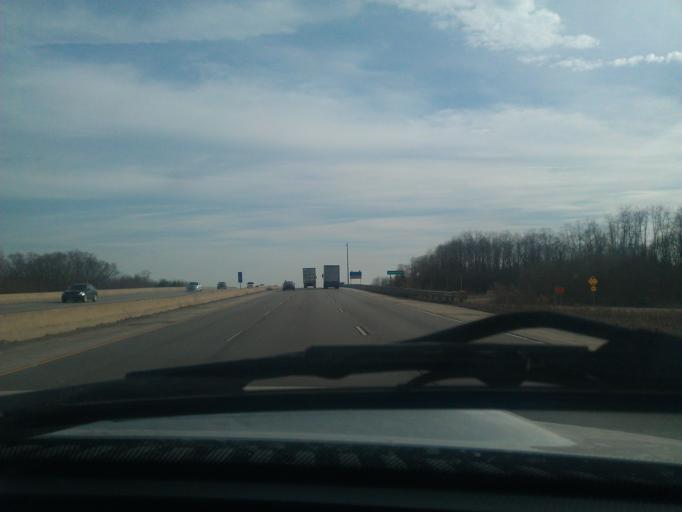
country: US
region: Wisconsin
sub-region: Kenosha County
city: Somers
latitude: 42.6720
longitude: -87.9531
